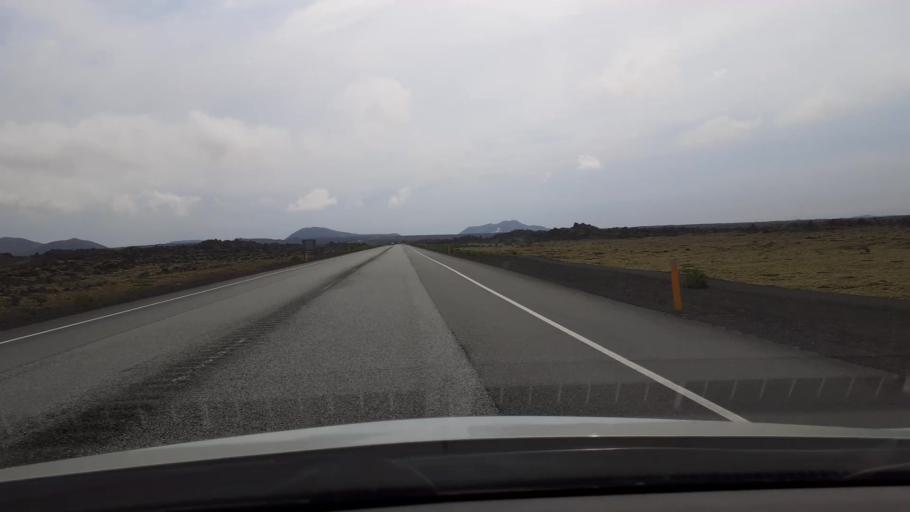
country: IS
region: Southern Peninsula
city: Vogar
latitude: 63.9353
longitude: -22.4272
